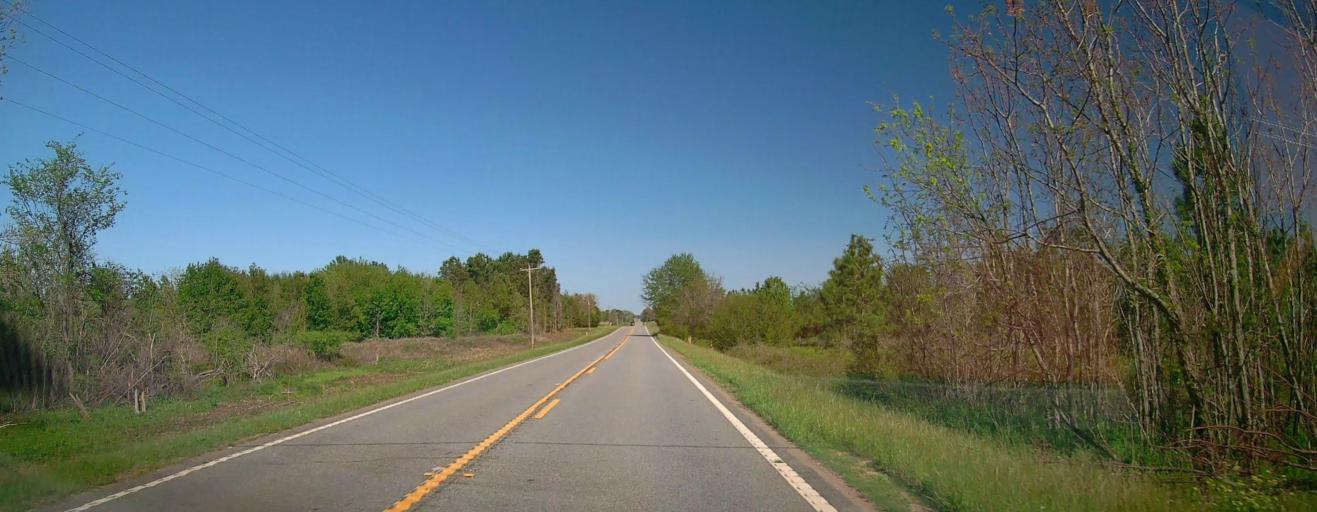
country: US
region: Georgia
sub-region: Dooly County
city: Unadilla
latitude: 32.2602
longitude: -83.7008
